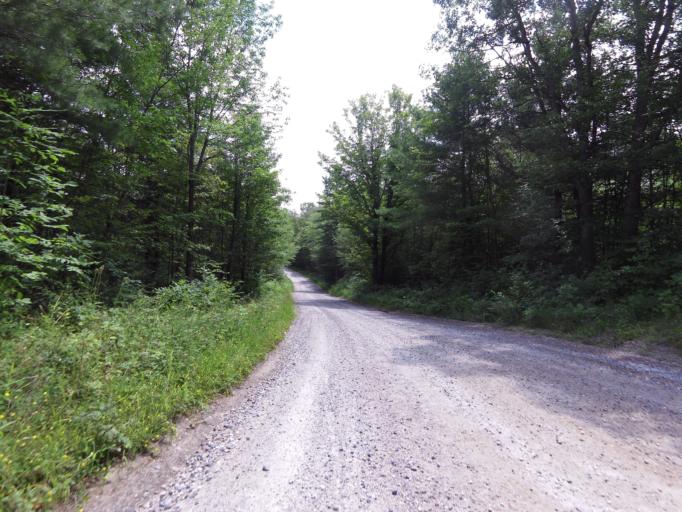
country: CA
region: Ontario
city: Perth
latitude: 44.7821
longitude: -76.6099
